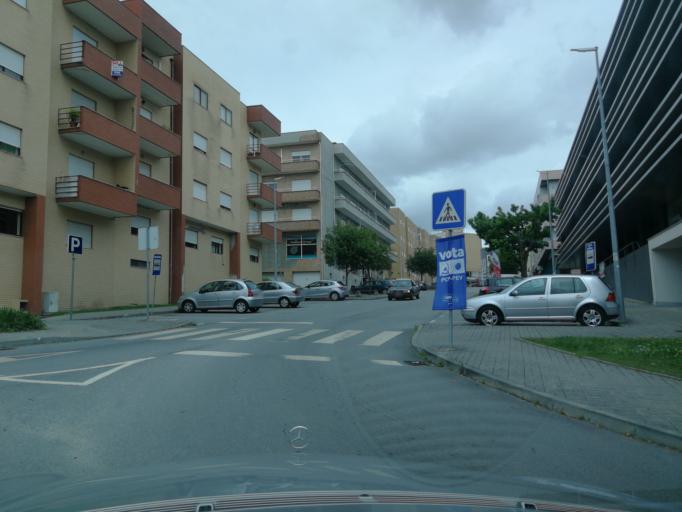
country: PT
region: Braga
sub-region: Amares
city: Amares
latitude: 41.6259
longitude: -8.3627
